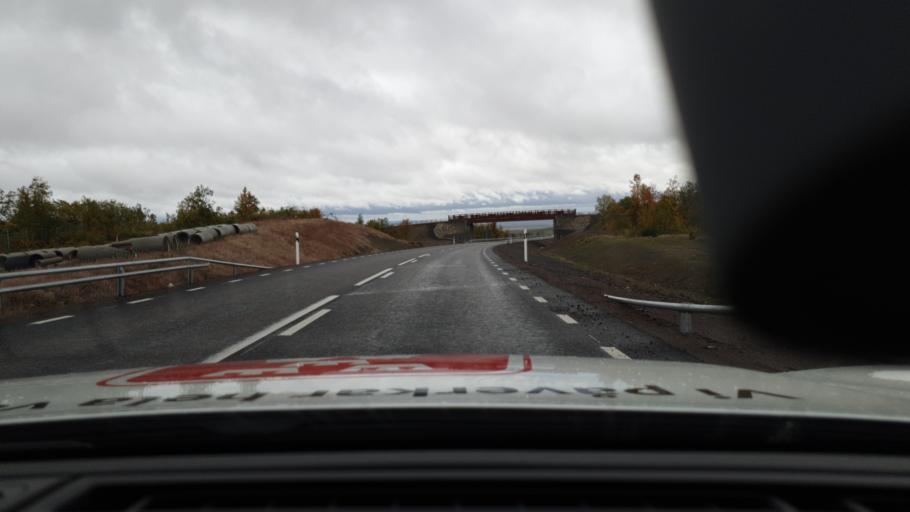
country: SE
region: Norrbotten
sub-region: Kiruna Kommun
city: Kiruna
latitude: 67.8683
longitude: 20.2263
